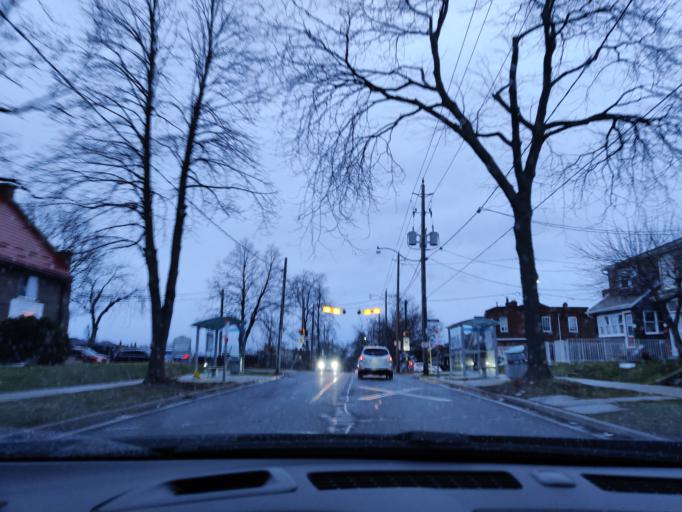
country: CA
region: Ontario
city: Toronto
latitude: 43.6814
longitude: -79.4574
